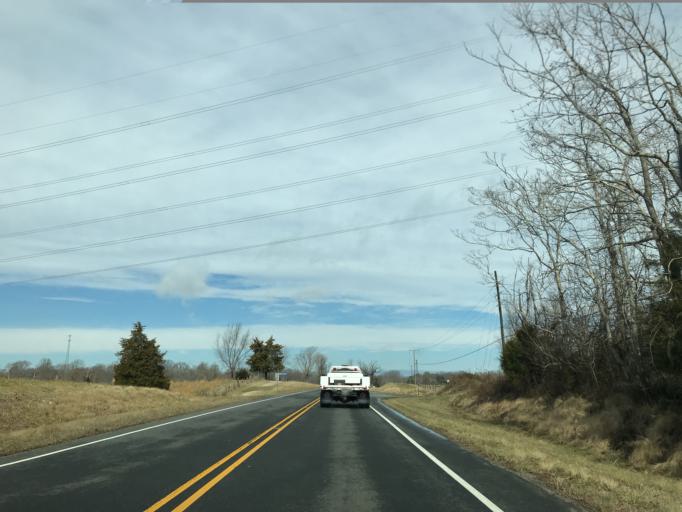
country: US
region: Virginia
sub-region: King George County
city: Dahlgren
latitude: 38.3253
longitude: -77.0816
